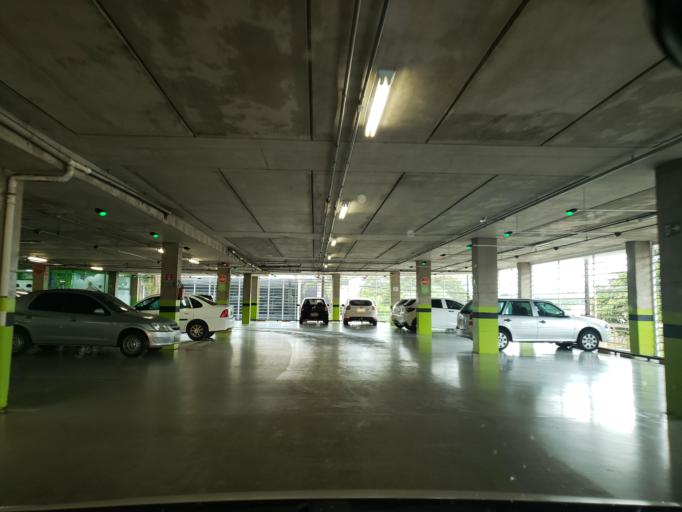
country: BR
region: Sao Paulo
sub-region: Bauru
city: Bauru
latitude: -22.3398
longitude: -49.0449
